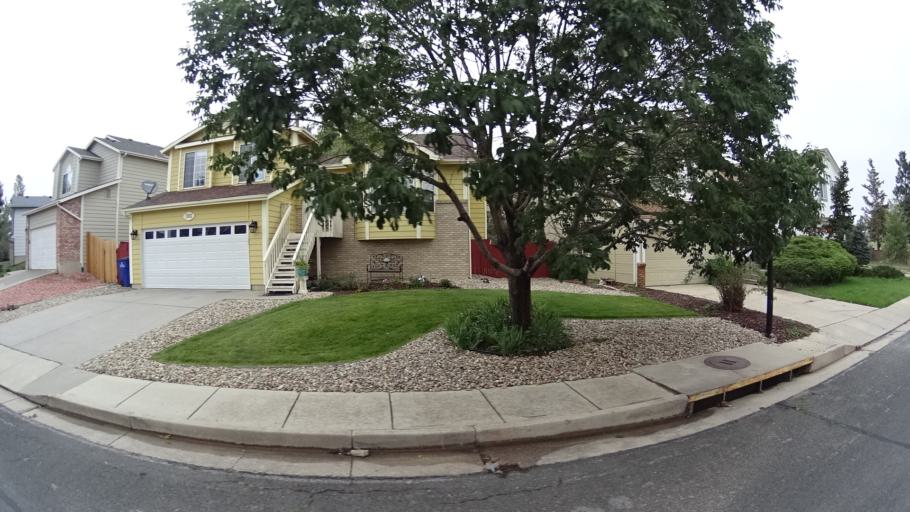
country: US
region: Colorado
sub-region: El Paso County
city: Cimarron Hills
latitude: 38.9199
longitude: -104.7242
